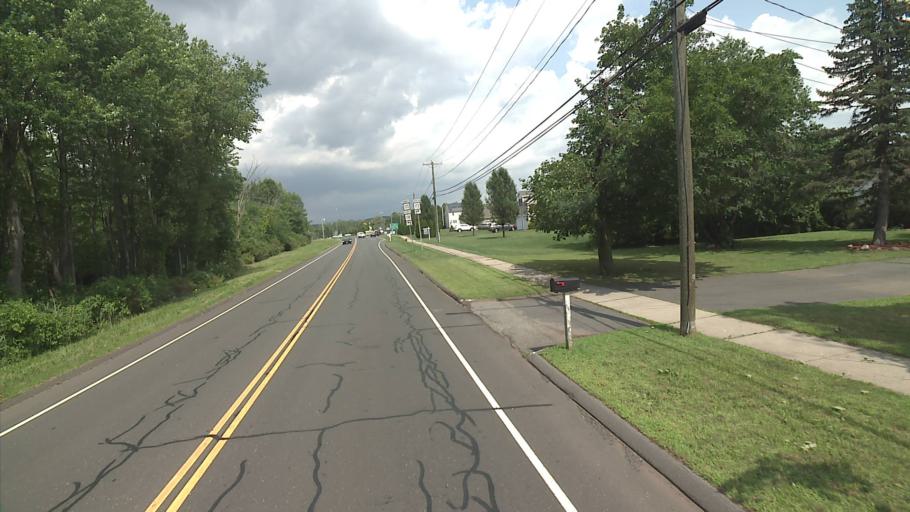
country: US
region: Connecticut
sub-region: Hartford County
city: Newington
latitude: 41.6749
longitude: -72.7315
